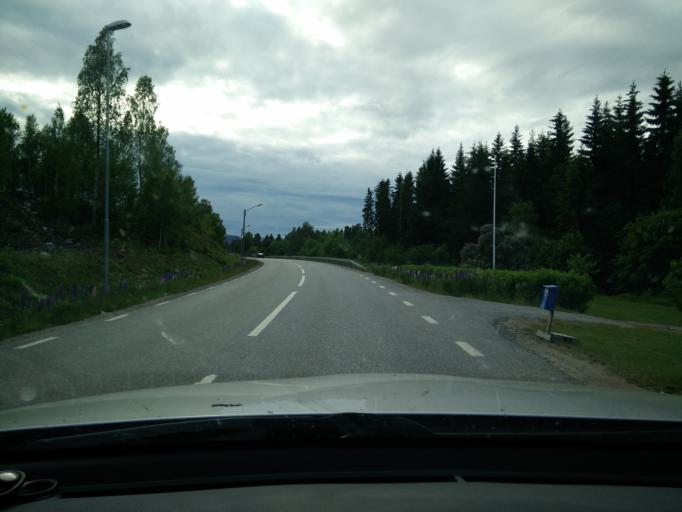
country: SE
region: Gaevleborg
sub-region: Nordanstigs Kommun
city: Bergsjoe
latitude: 62.0993
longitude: 16.7432
